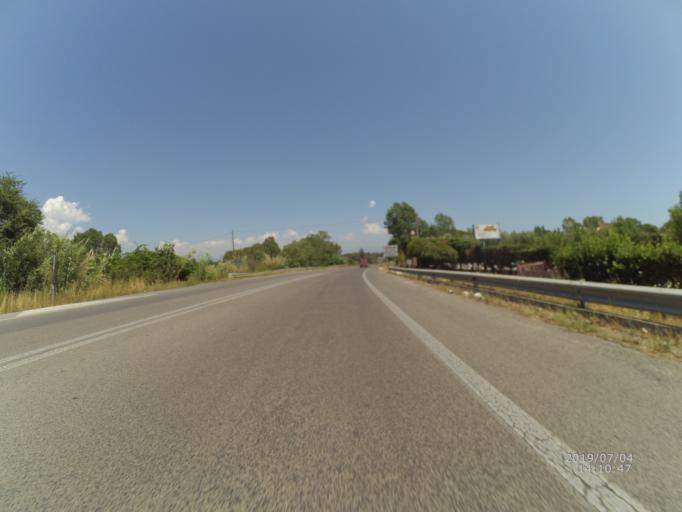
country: IT
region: Latium
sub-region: Provincia di Latina
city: Terracina
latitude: 41.2994
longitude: 13.2797
